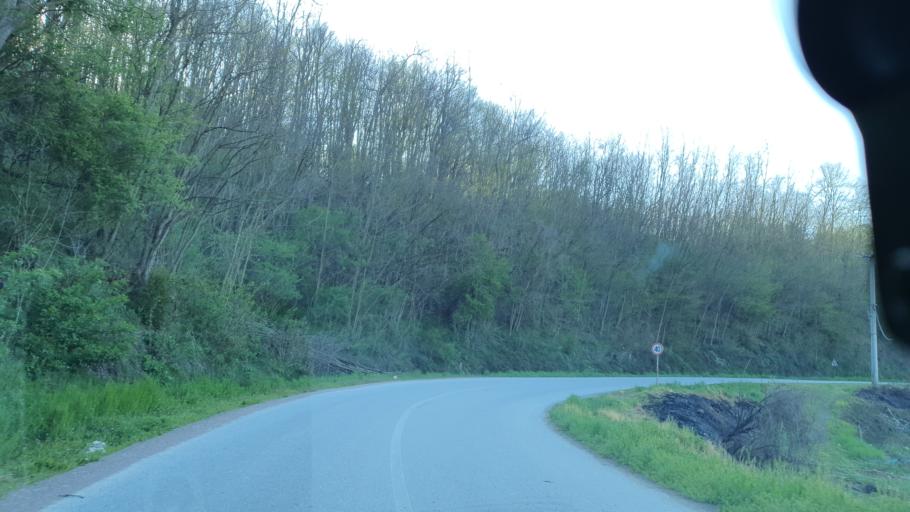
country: RS
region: Central Serbia
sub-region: Kolubarski Okrug
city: Osecina
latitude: 44.3228
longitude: 19.5257
